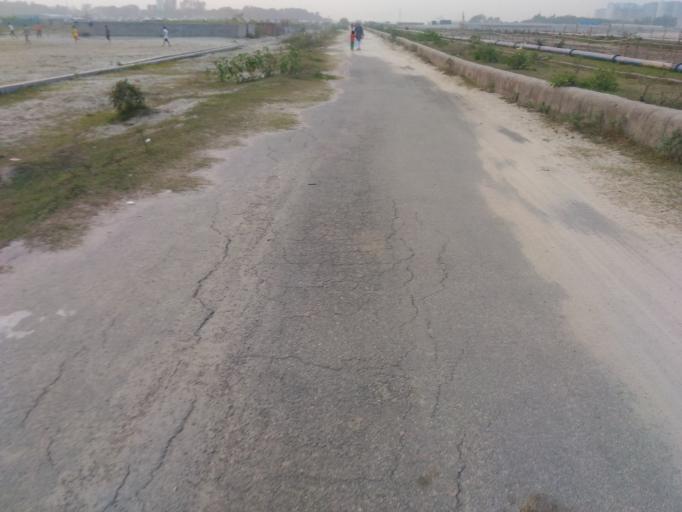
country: BD
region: Dhaka
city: Tungi
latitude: 23.8466
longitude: 90.3667
